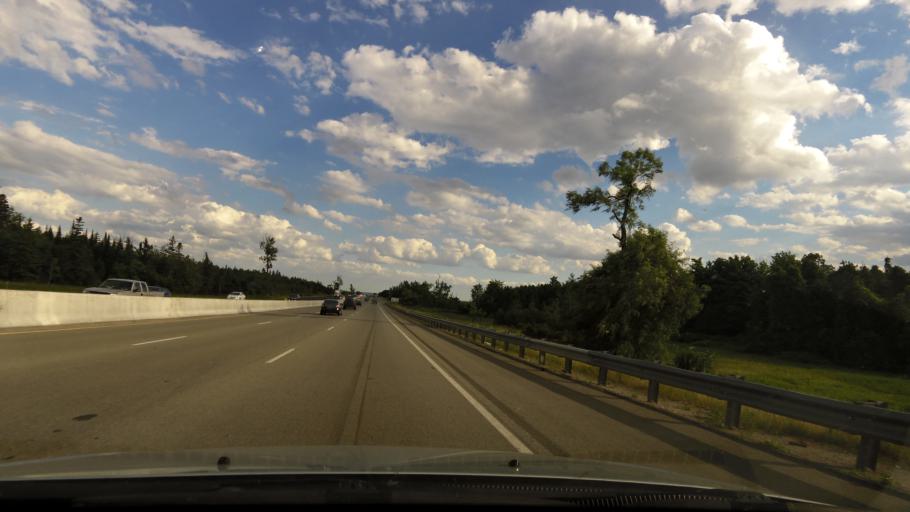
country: CA
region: Ontario
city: Bradford West Gwillimbury
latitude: 44.1432
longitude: -79.6417
